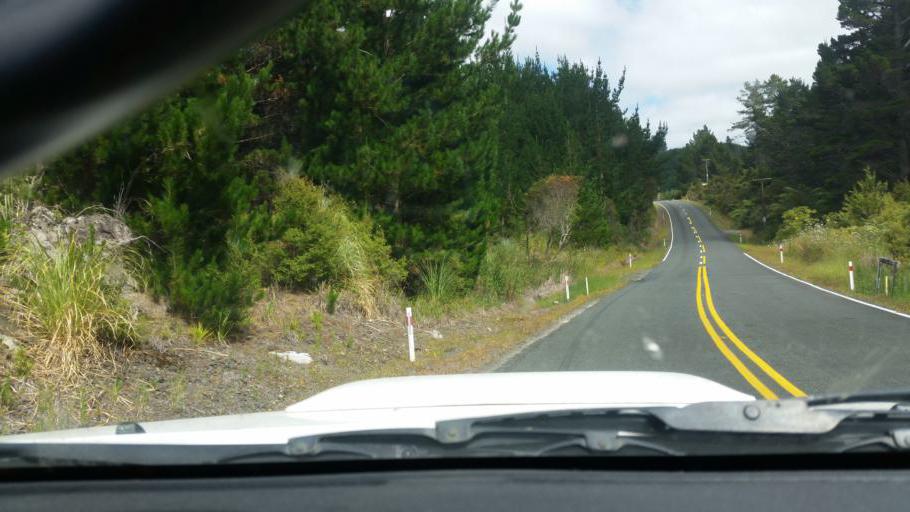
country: NZ
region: Northland
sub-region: Kaipara District
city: Dargaville
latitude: -35.8166
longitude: 173.7237
